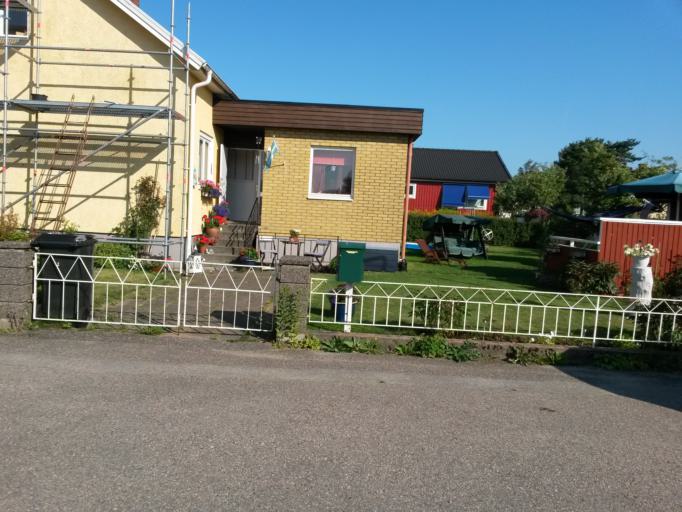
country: SE
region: Vaestra Goetaland
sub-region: Vargarda Kommun
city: Vargarda
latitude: 58.0379
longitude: 12.8132
